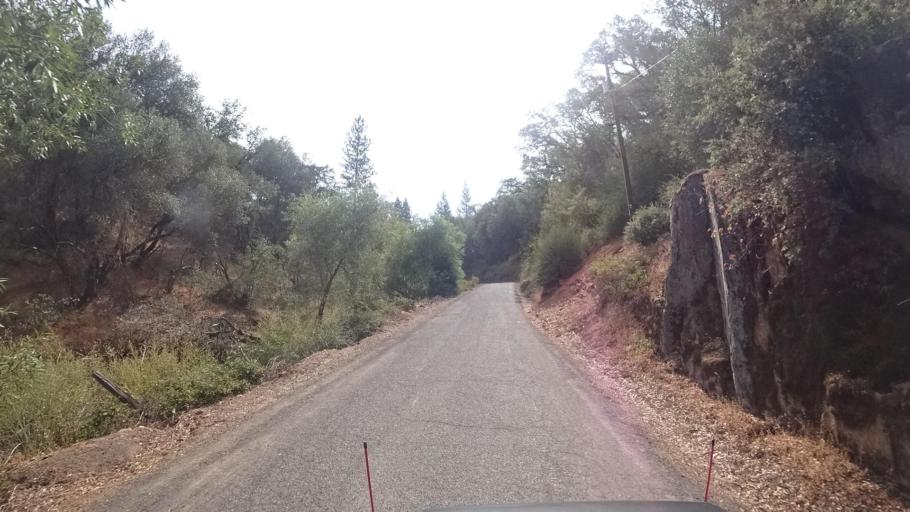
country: US
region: California
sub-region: Mariposa County
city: Midpines
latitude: 37.5629
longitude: -119.9733
